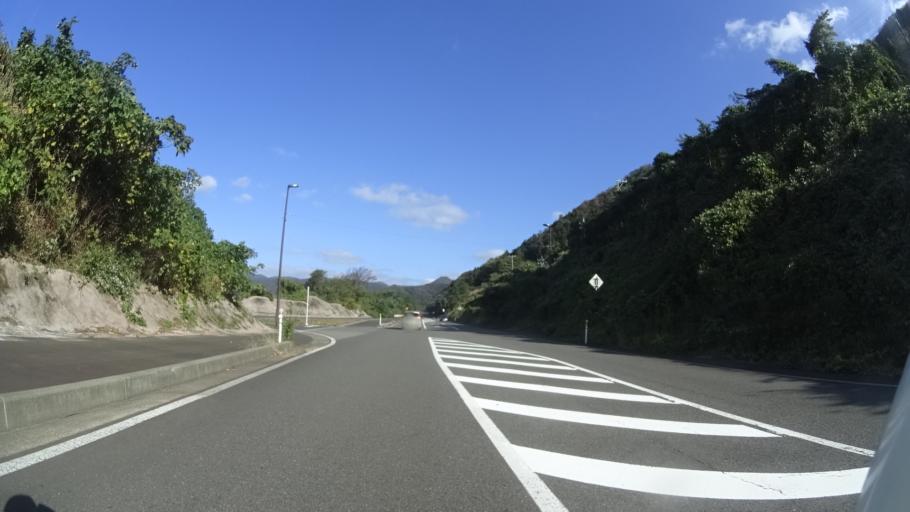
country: JP
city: Asahi
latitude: 35.9187
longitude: 135.9985
